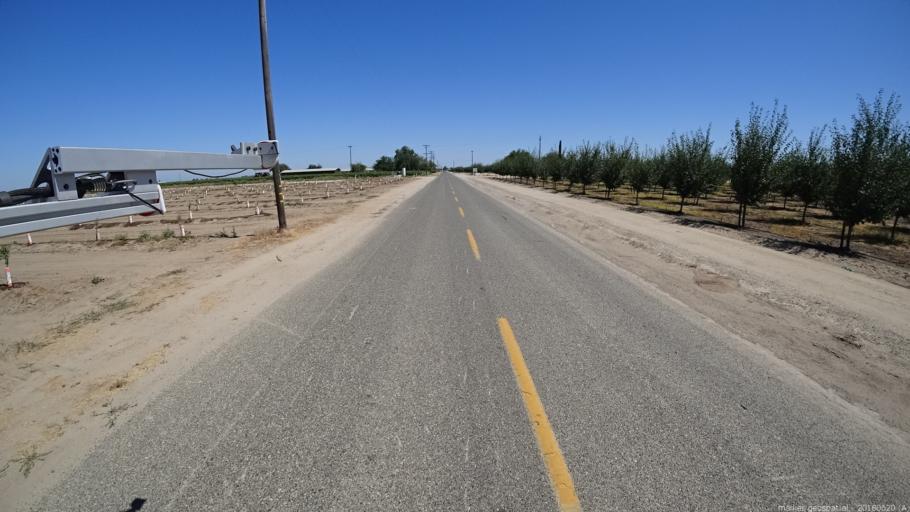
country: US
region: California
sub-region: Fresno County
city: Biola
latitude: 36.8431
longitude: -120.0192
